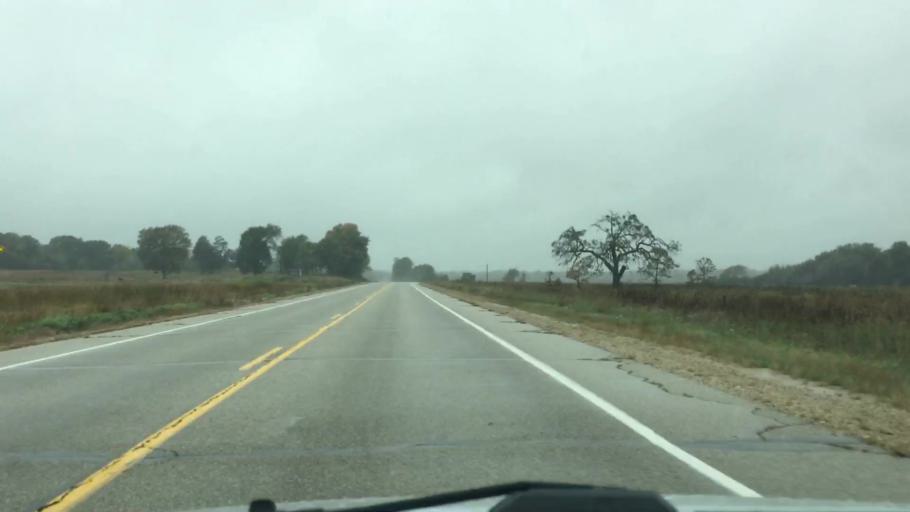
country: US
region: Wisconsin
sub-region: Waukesha County
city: Eagle
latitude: 42.8792
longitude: -88.5218
